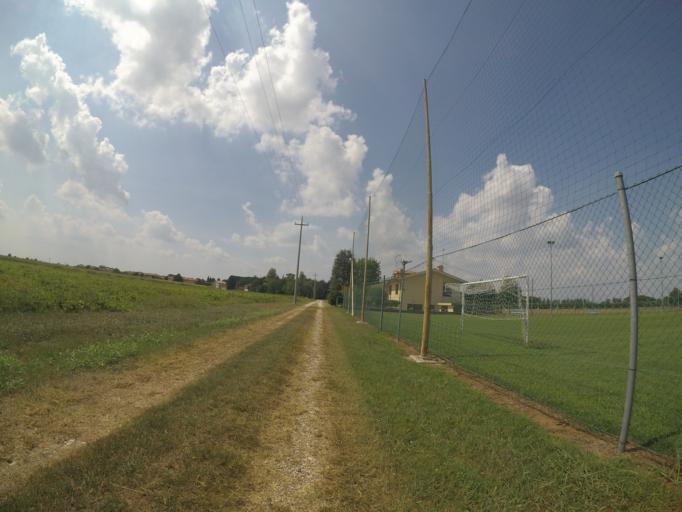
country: IT
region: Friuli Venezia Giulia
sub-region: Provincia di Udine
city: Bertiolo
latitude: 45.9499
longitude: 13.0184
